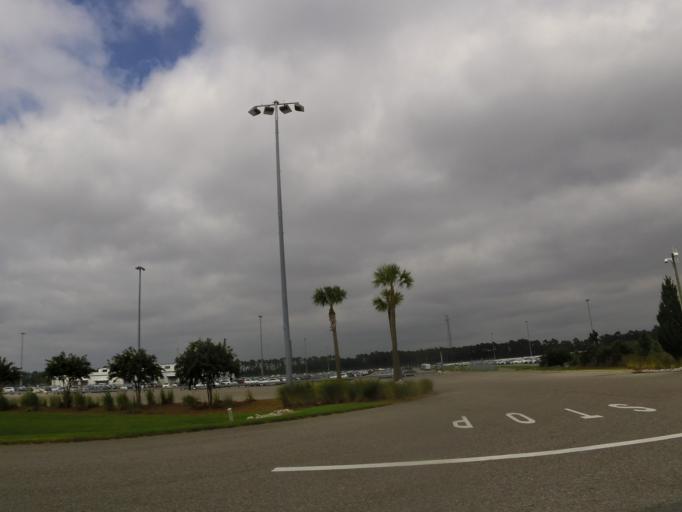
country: US
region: Georgia
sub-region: Glynn County
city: Brunswick
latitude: 31.1089
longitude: -81.5400
